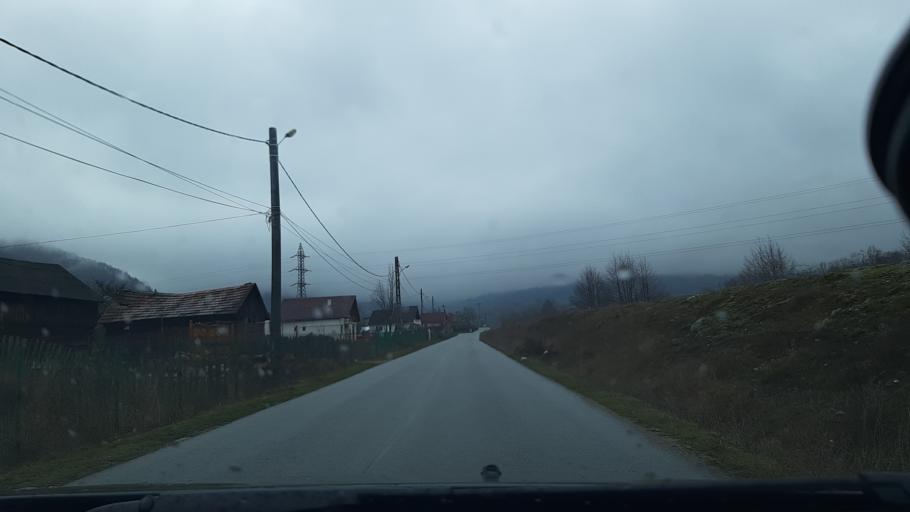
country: RO
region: Hunedoara
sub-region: Oras Petrila
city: Petrila
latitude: 45.4286
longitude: 23.4220
